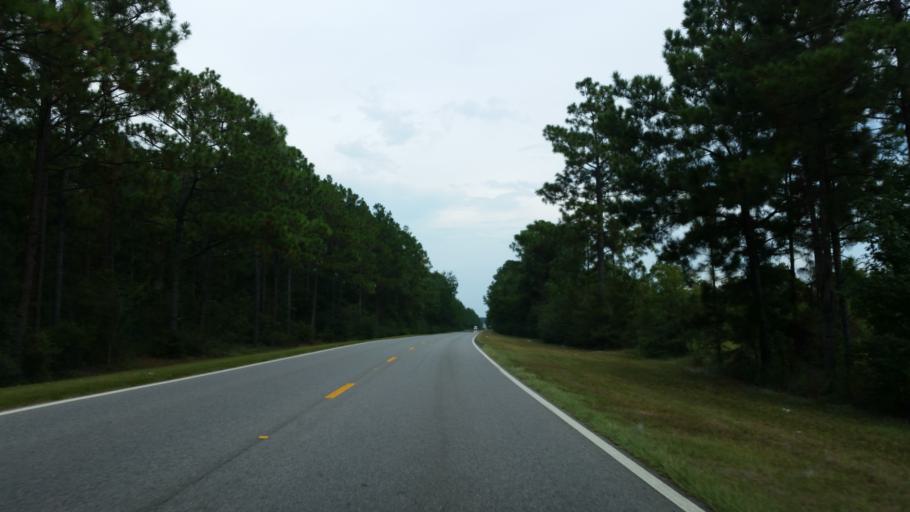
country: US
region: Florida
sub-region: Santa Rosa County
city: Wallace
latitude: 30.6732
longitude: -87.2533
